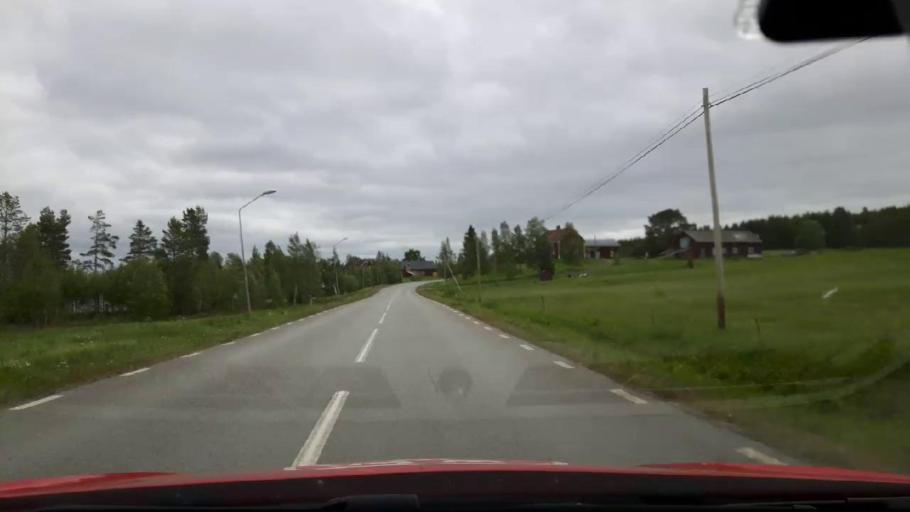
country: SE
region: Jaemtland
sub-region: OEstersunds Kommun
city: Lit
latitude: 63.6808
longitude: 15.0415
